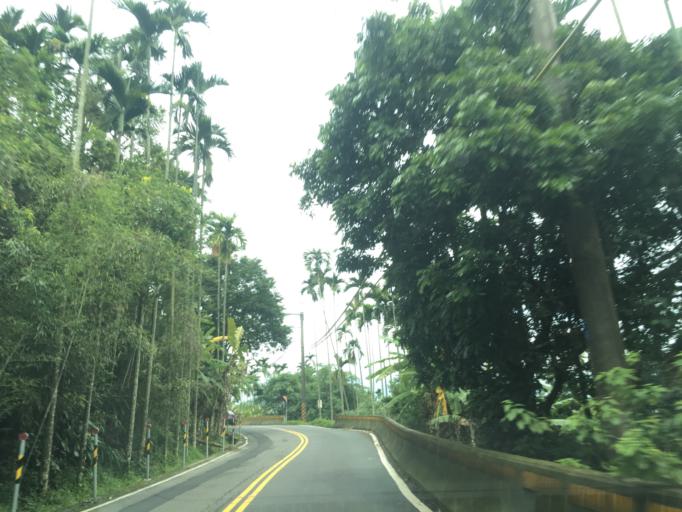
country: TW
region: Taiwan
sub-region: Yunlin
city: Douliu
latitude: 23.5631
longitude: 120.5741
